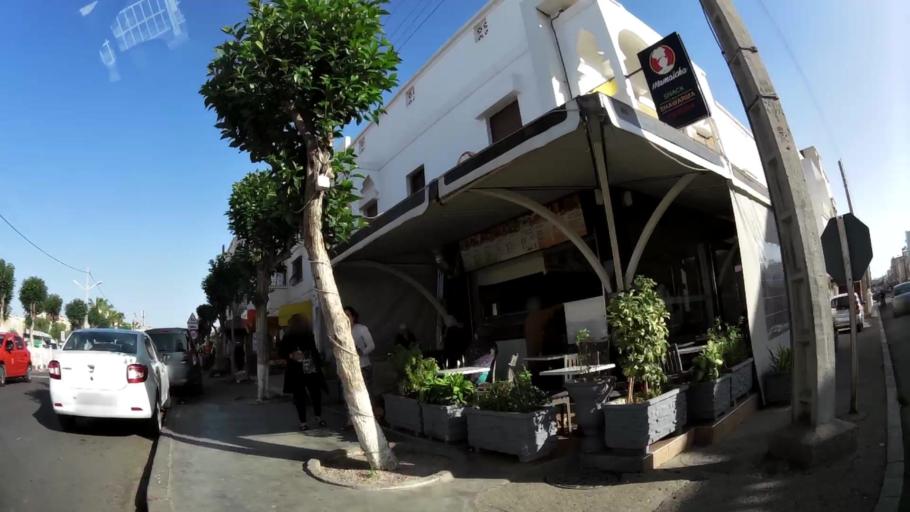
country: MA
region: Souss-Massa-Draa
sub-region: Agadir-Ida-ou-Tnan
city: Agadir
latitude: 30.4307
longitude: -9.5770
